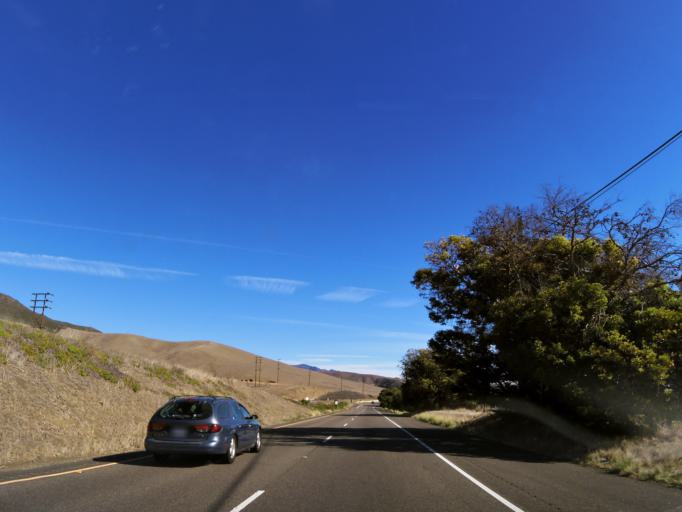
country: US
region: California
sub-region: Santa Barbara County
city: Solvang
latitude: 34.4735
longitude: -120.1559
